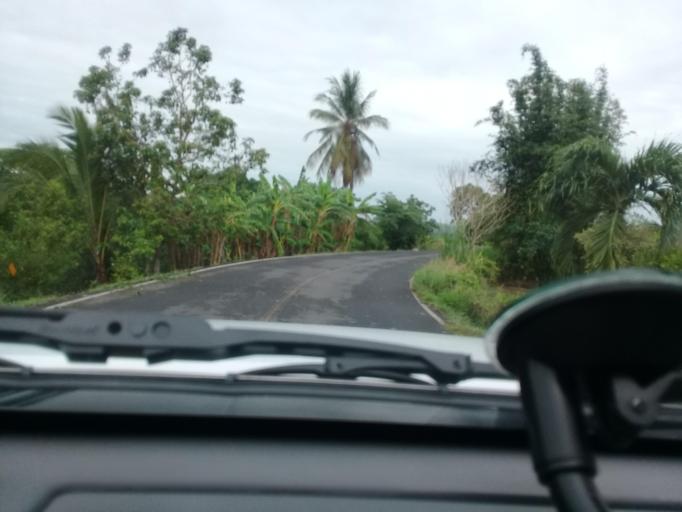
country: MX
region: Veracruz
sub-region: Paso de Ovejas
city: El Hatito
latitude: 19.3203
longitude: -96.3895
